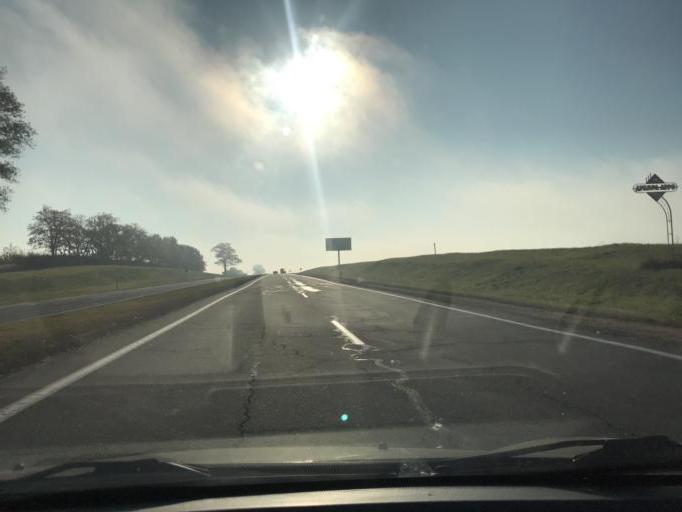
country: BY
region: Minsk
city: Dukora
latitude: 53.6878
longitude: 27.9088
